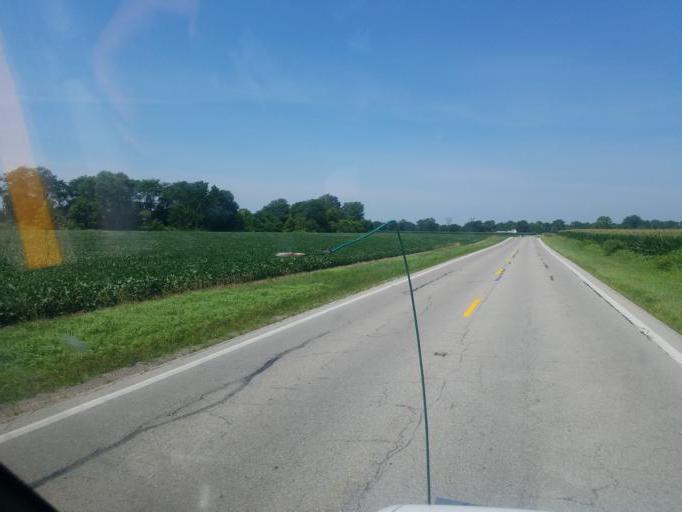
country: US
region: Ohio
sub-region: Logan County
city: West Liberty
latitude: 40.2511
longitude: -83.7382
